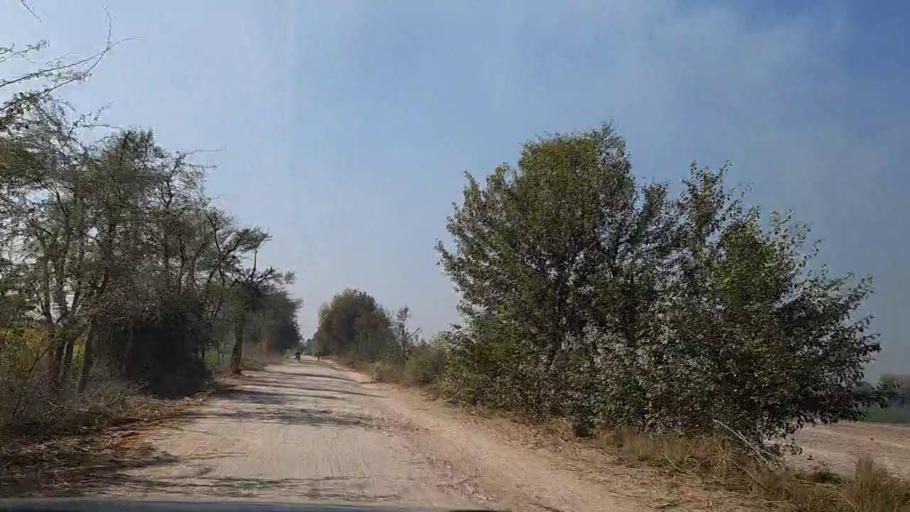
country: PK
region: Sindh
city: Daulatpur
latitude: 26.2905
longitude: 68.0704
